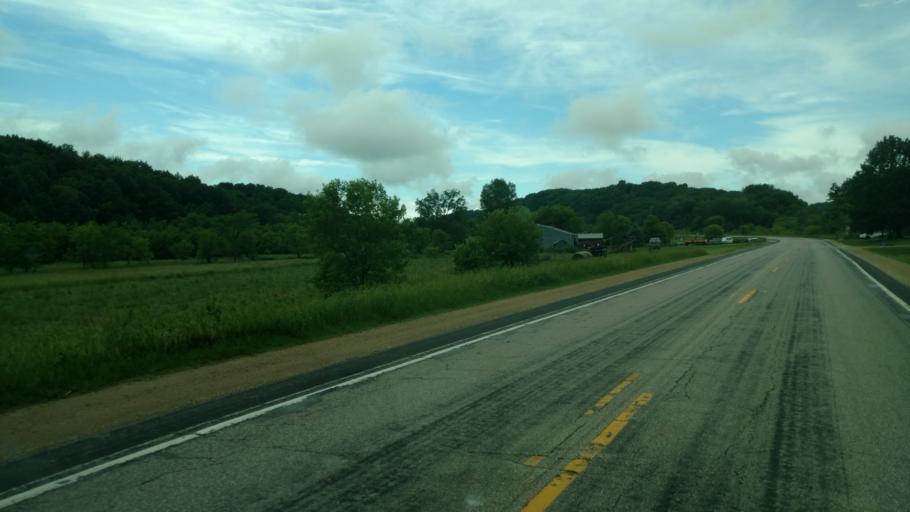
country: US
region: Wisconsin
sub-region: Vernon County
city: Hillsboro
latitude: 43.6582
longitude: -90.3975
